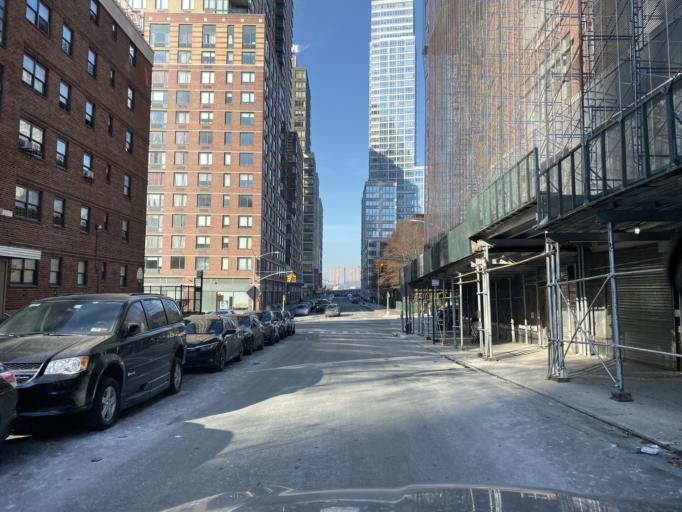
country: US
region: New Jersey
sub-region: Hudson County
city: Guttenberg
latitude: 40.7739
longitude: -73.9882
